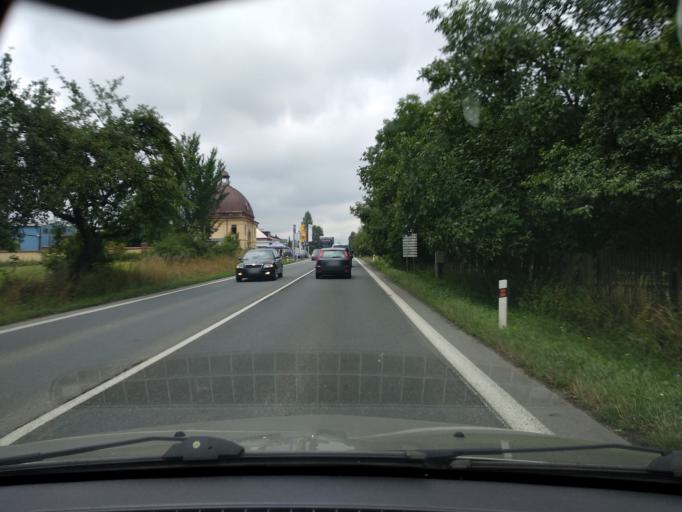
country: CZ
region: Olomoucky
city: Dolni Studenky
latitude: 49.9474
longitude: 16.9543
